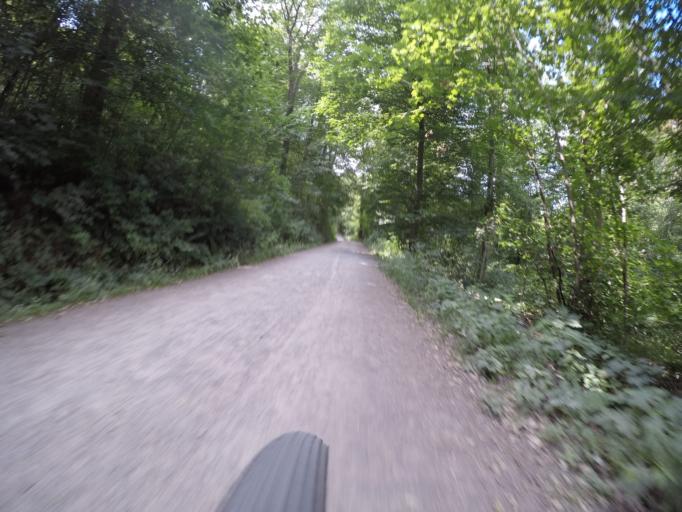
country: DE
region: Baden-Wuerttemberg
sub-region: Regierungsbezirk Stuttgart
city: Stuttgart Feuerbach
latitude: 48.7896
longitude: 9.1428
